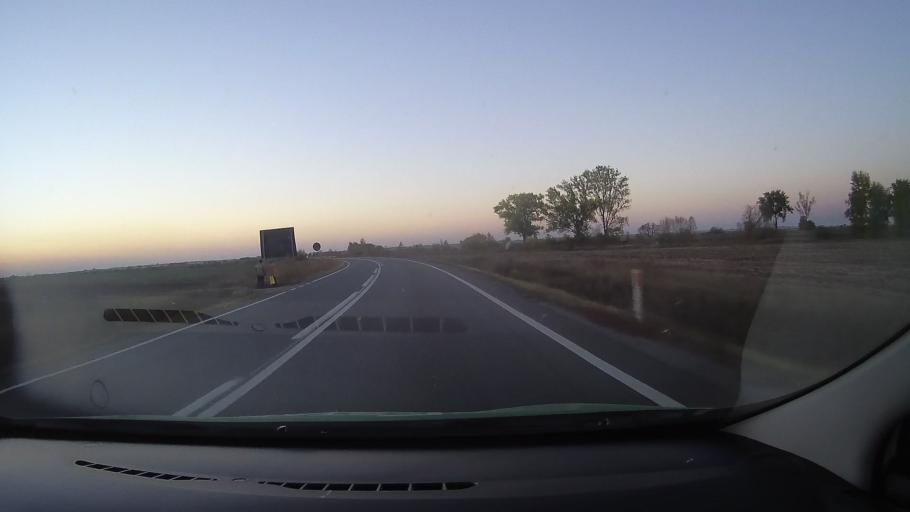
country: RO
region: Bihor
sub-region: Comuna Tarcea
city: Tarcea
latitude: 47.4337
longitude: 22.2044
